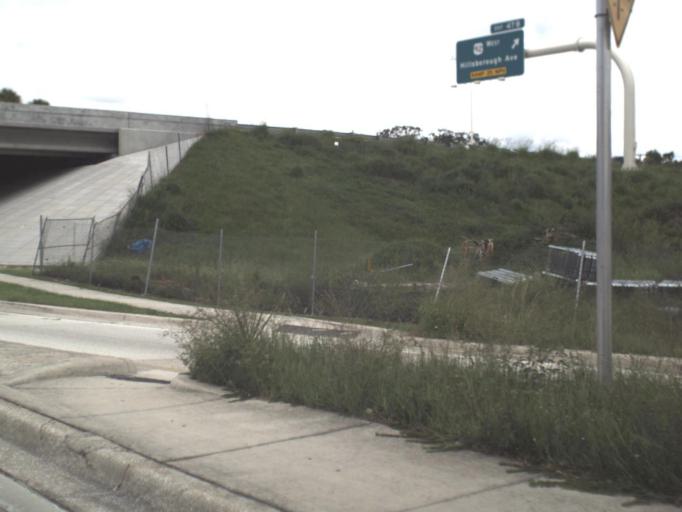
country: US
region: Florida
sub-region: Hillsborough County
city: Tampa
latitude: 27.9962
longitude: -82.4531
